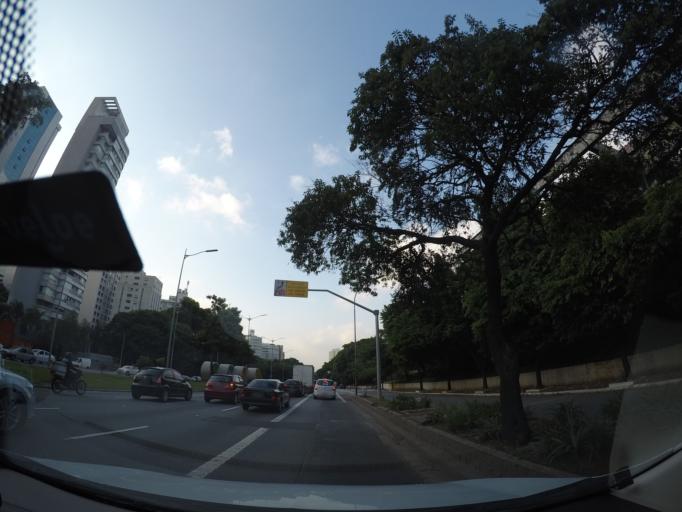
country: BR
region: Sao Paulo
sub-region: Sao Paulo
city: Sao Paulo
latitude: -23.5730
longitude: -46.6385
